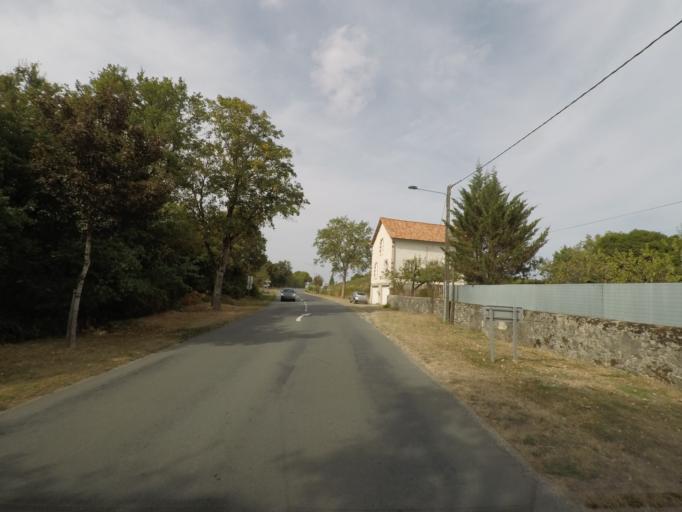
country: FR
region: Poitou-Charentes
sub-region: Departement de la Charente
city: Ruffec
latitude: 46.0355
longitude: 0.1967
